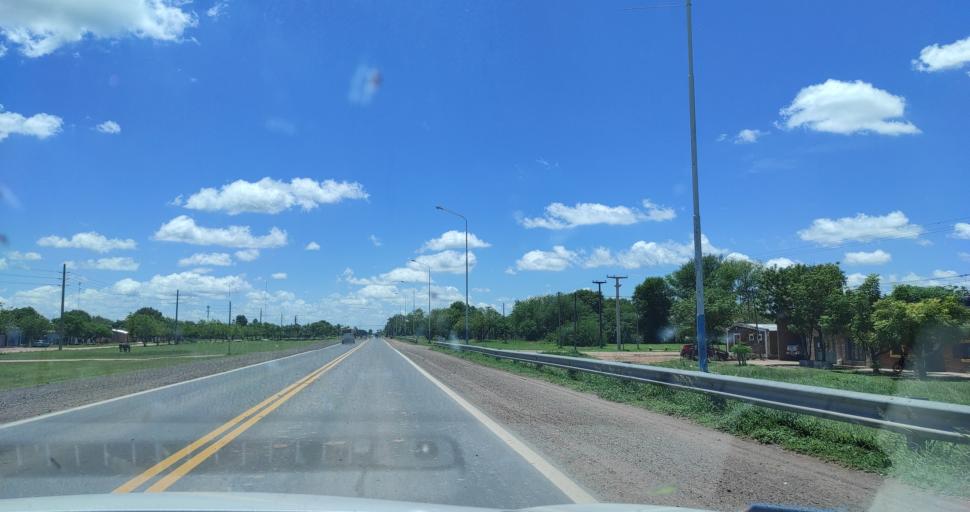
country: AR
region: Chaco
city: Campo Largo
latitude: -26.8085
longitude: -60.8392
